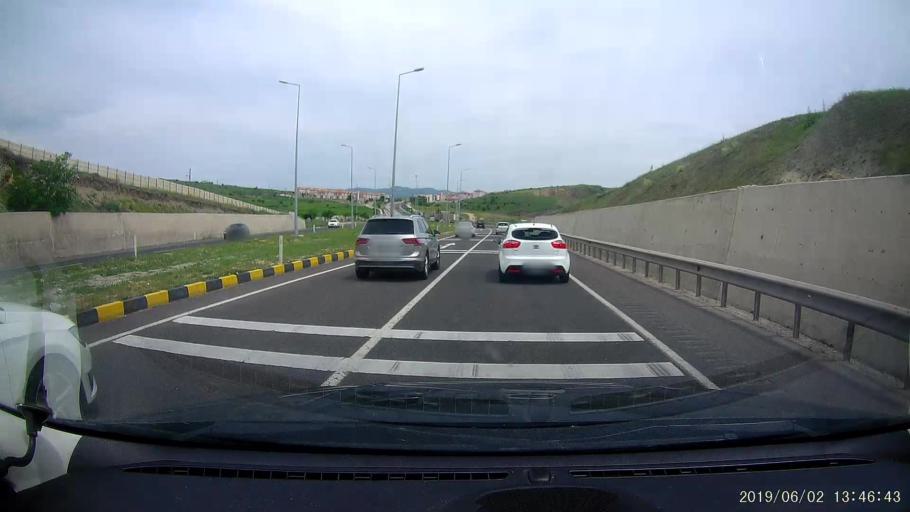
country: TR
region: Cankiri
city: Kursunlu
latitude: 40.8411
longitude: 33.2716
